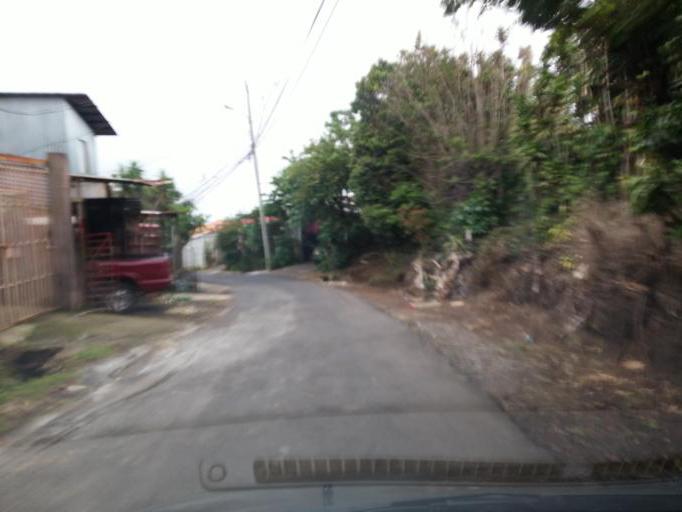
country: CR
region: Heredia
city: San Josecito
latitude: 10.0450
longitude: -84.1053
